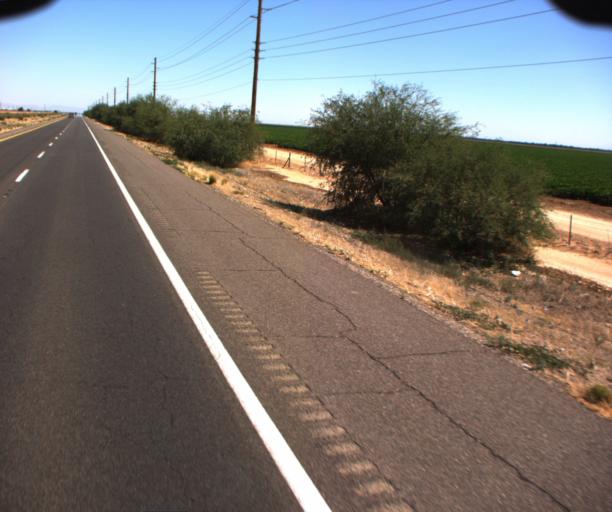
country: US
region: Arizona
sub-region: Pinal County
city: Maricopa
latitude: 32.9733
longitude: -112.0477
